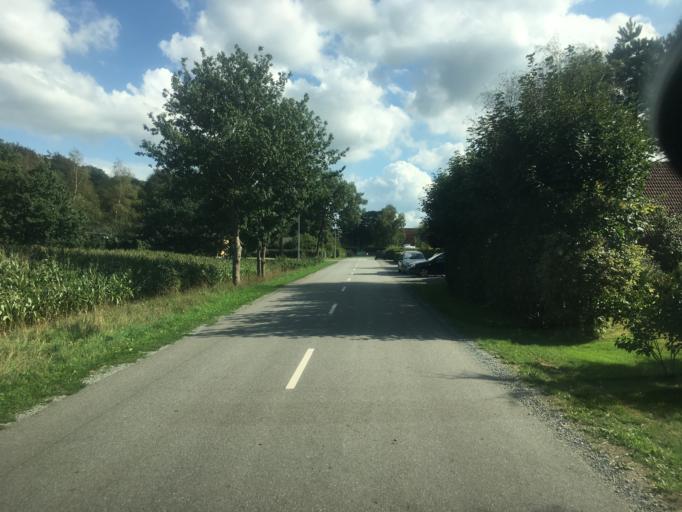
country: DE
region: Schleswig-Holstein
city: Ellhoft
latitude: 54.9497
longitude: 8.9645
